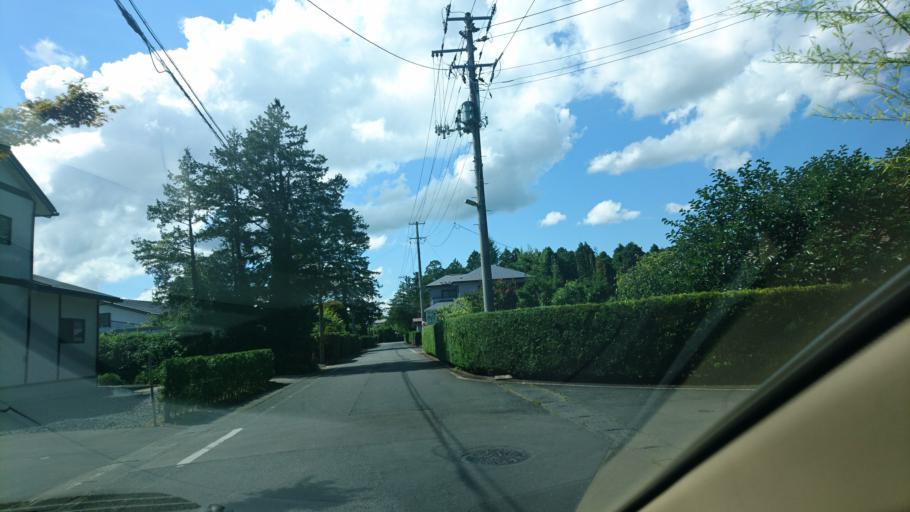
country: JP
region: Iwate
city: Mizusawa
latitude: 39.1951
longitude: 141.1215
